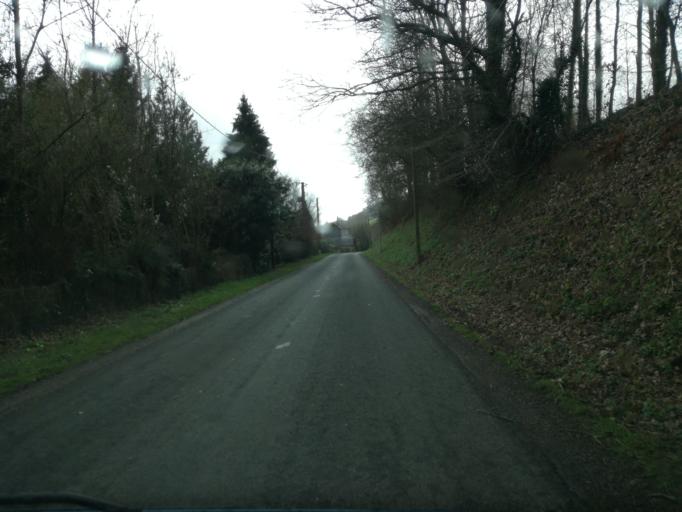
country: FR
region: Haute-Normandie
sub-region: Departement de la Seine-Maritime
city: Saint-Wandrille-Rancon
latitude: 49.5424
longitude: 0.7555
